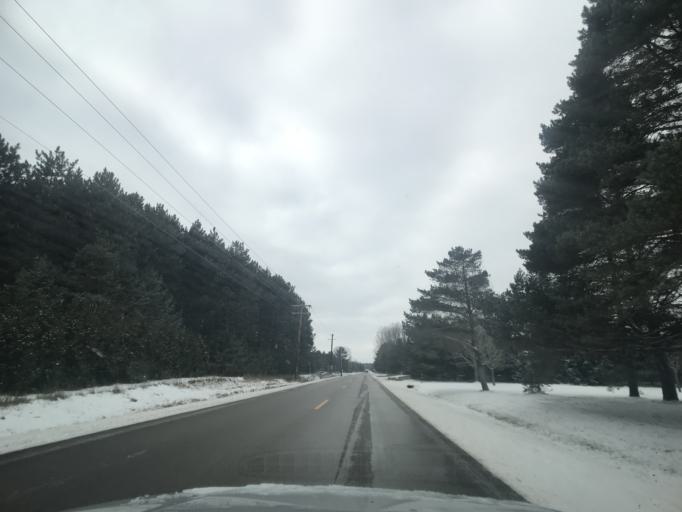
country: US
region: Wisconsin
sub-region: Brown County
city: Suamico
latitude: 44.6918
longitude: -88.1092
